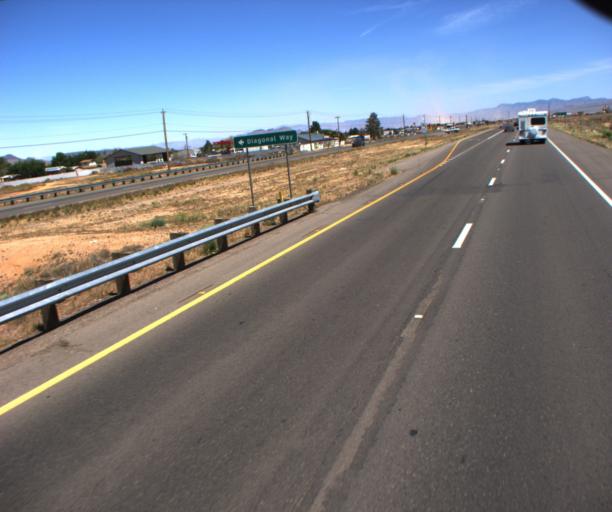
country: US
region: Arizona
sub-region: Mohave County
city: New Kingman-Butler
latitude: 35.2440
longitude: -113.9847
